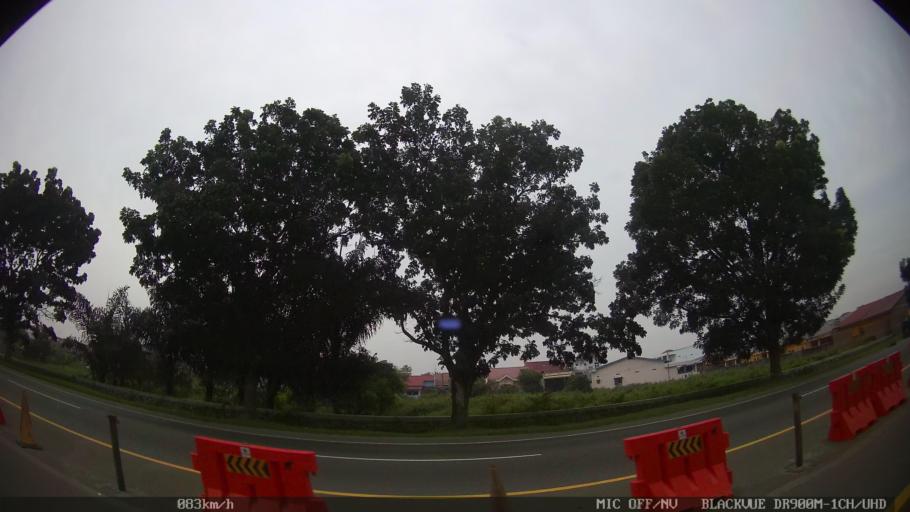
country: ID
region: North Sumatra
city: Medan
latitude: 3.5626
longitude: 98.7257
